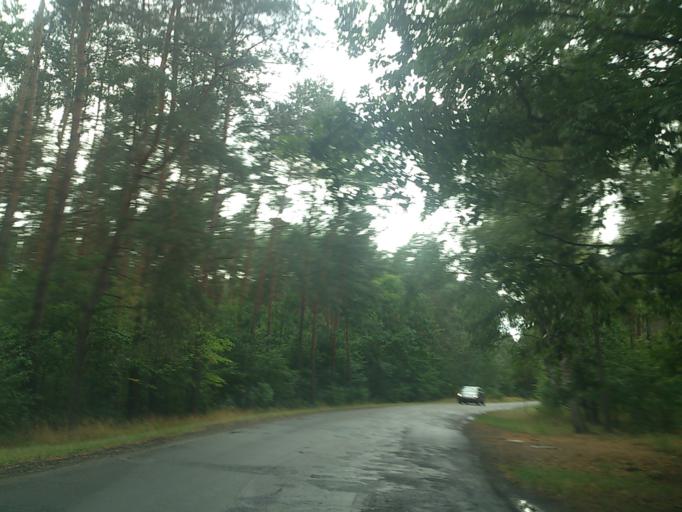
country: PL
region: Greater Poland Voivodeship
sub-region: Powiat poznanski
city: Kobylnica
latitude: 52.5191
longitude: 17.1614
